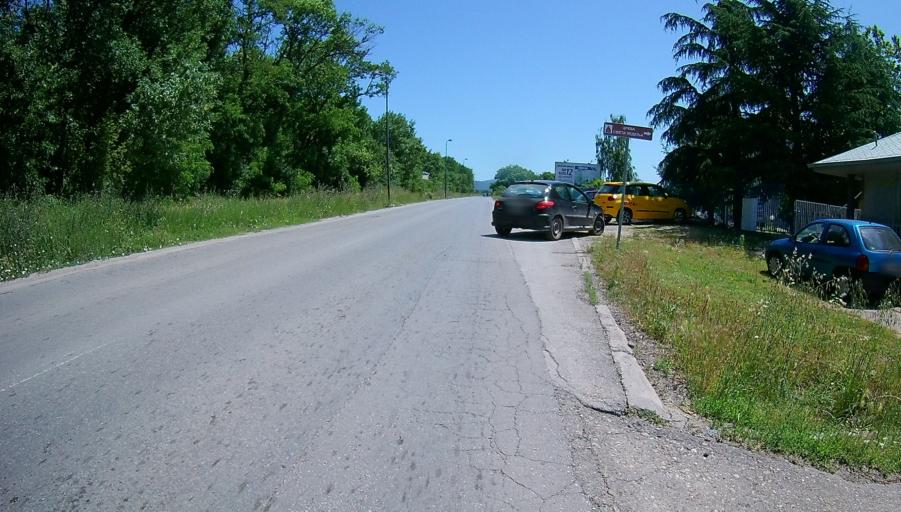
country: RS
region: Central Serbia
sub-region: Nisavski Okrug
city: Nis
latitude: 43.3007
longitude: 21.8743
